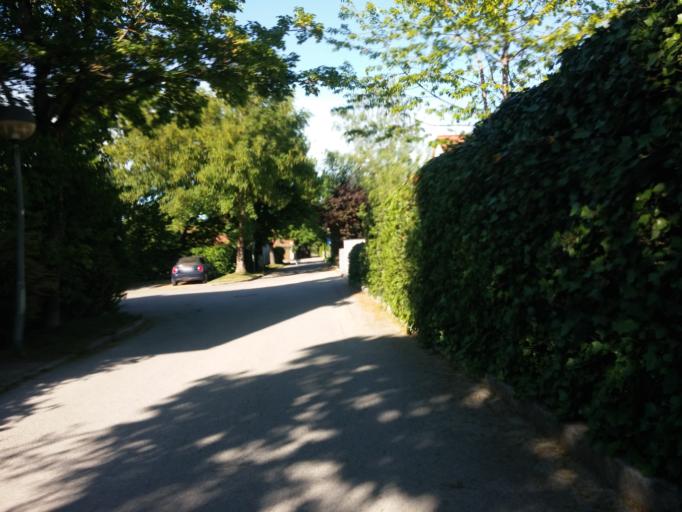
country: DE
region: Bavaria
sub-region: Upper Bavaria
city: Vaterstetten
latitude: 48.1088
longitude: 11.7682
